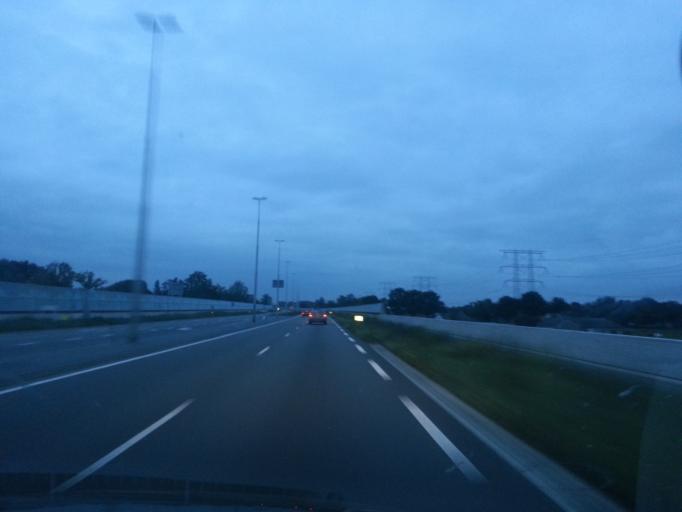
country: NL
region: North Brabant
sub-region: Gemeente Tilburg
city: Tilburg
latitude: 51.5757
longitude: 5.1257
